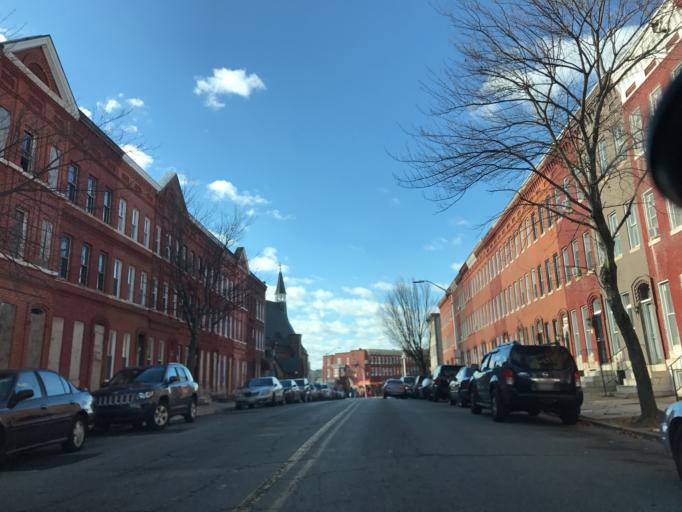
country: US
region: Maryland
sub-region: City of Baltimore
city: Baltimore
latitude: 39.2977
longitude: -76.6321
